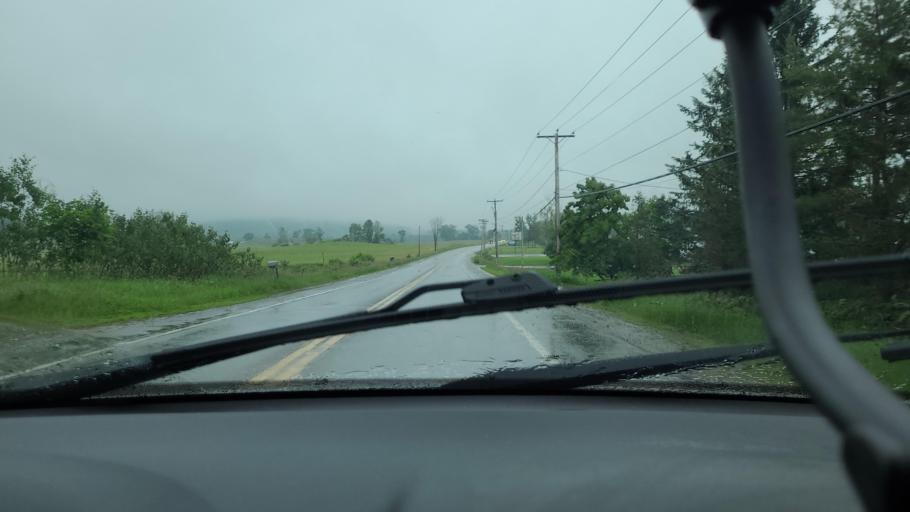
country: CA
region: Quebec
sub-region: Outaouais
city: Saint-Andre-Avellin
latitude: 45.6842
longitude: -75.0423
